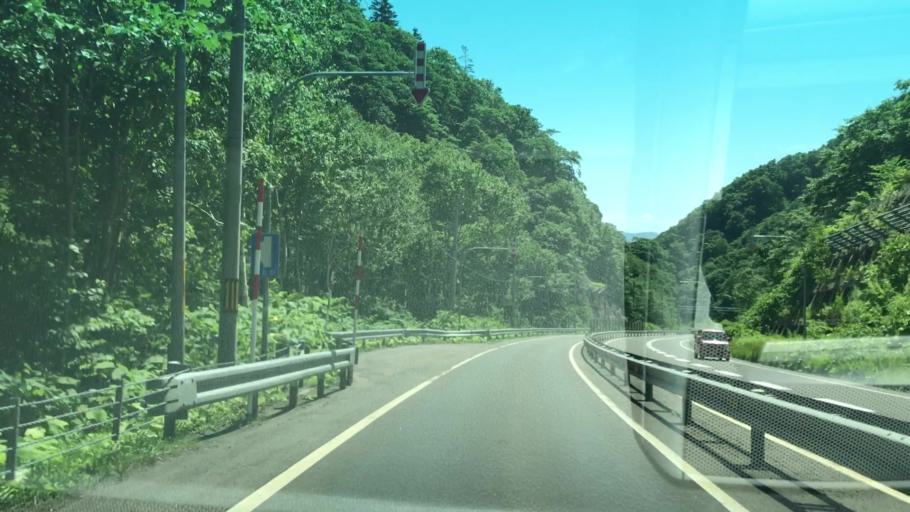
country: JP
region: Hokkaido
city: Yoichi
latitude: 43.0439
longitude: 140.6813
